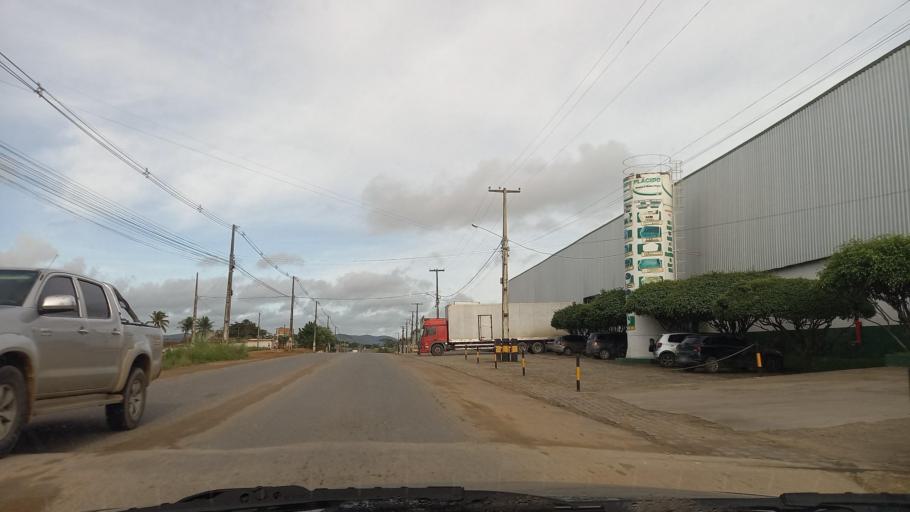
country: BR
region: Pernambuco
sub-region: Vitoria De Santo Antao
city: Vitoria de Santo Antao
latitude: -8.1221
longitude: -35.3327
